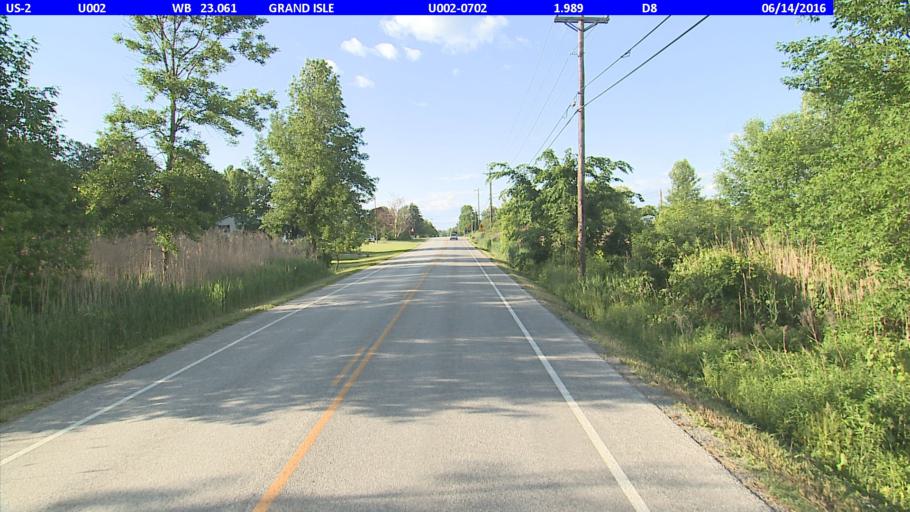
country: US
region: Vermont
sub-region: Grand Isle County
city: North Hero
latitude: 44.7388
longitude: -73.2899
